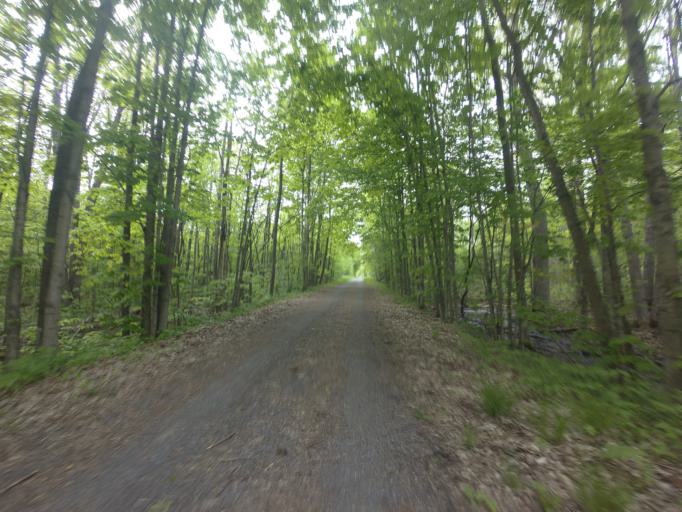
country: CA
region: Ontario
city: Kingston
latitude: 44.3403
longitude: -76.5975
